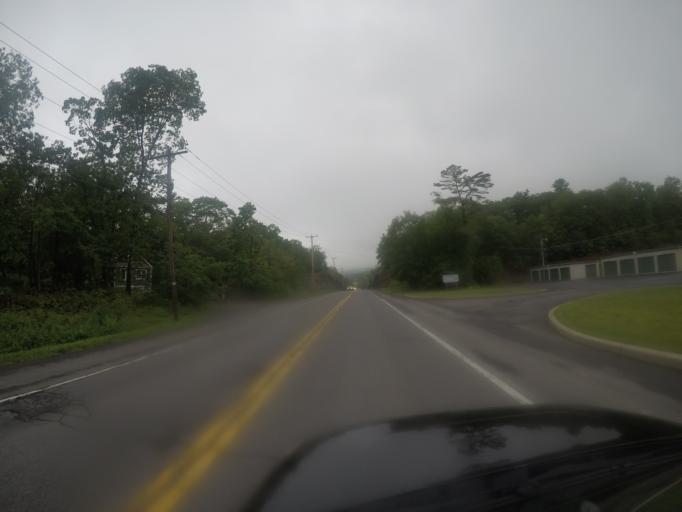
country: US
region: New York
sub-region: Ulster County
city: West Hurley
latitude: 42.0001
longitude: -74.1168
